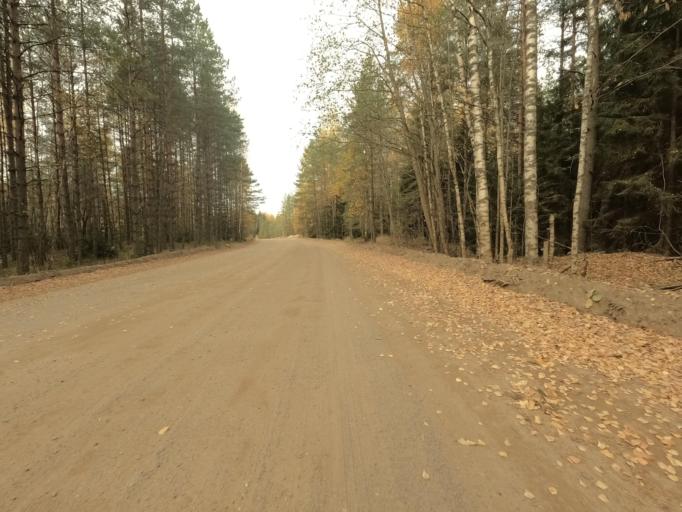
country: RU
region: Leningrad
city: Priladozhskiy
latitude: 59.6871
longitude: 31.3619
